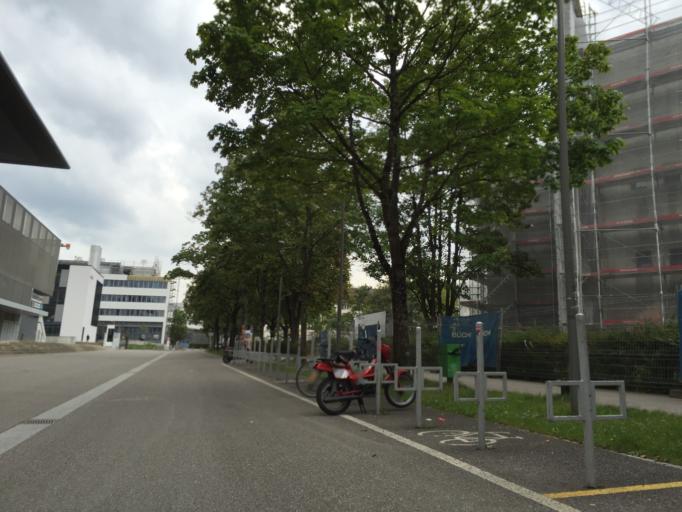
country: CH
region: Bern
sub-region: Bern-Mittelland District
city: Bern
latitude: 46.9641
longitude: 7.4634
